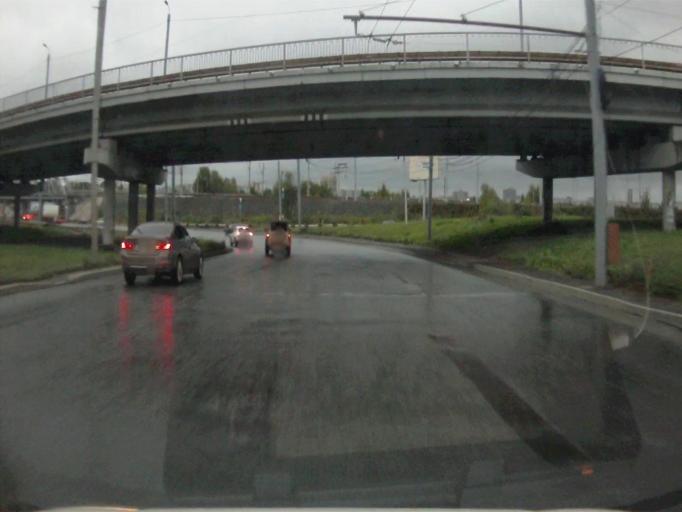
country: RU
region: Chelyabinsk
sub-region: Gorod Chelyabinsk
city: Chelyabinsk
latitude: 55.1569
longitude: 61.4440
